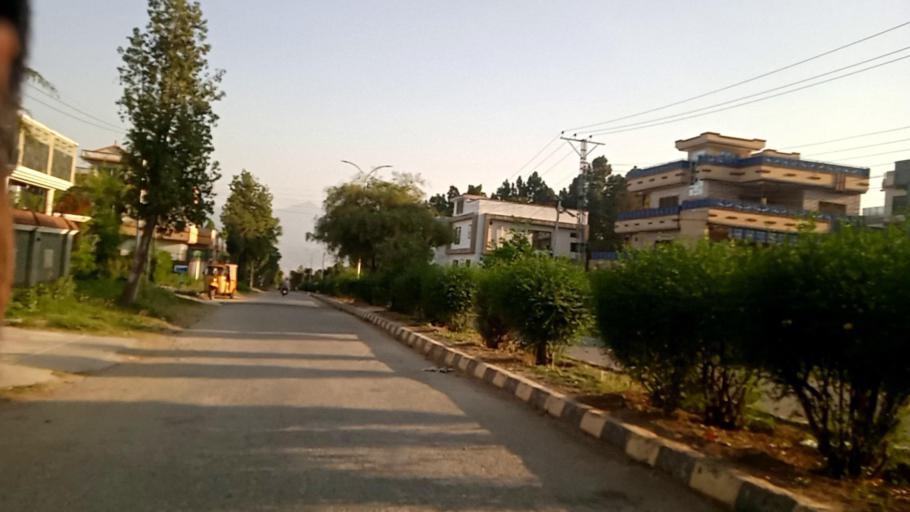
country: PK
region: Khyber Pakhtunkhwa
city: Mingora
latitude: 34.8326
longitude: 72.3421
